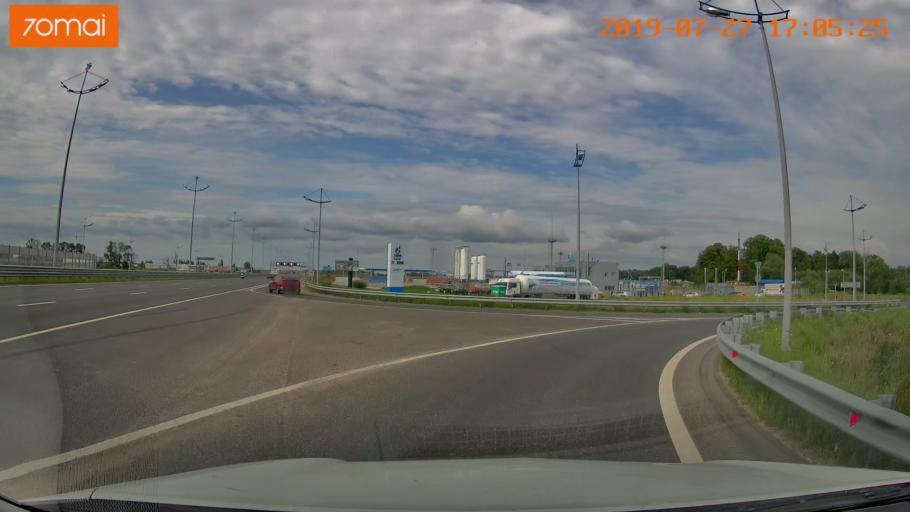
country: RU
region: Kaliningrad
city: Bol'shoe Isakovo
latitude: 54.7250
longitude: 20.5983
